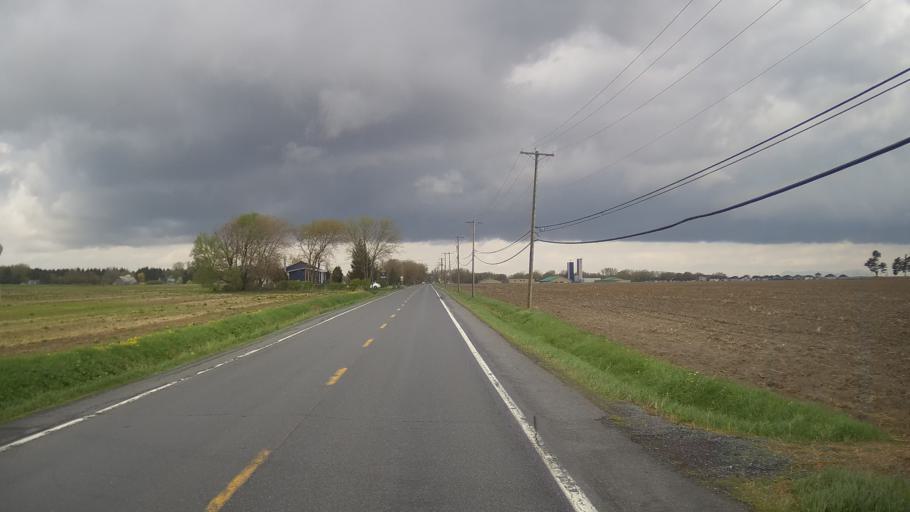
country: CA
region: Quebec
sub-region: Monteregie
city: Farnham
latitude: 45.3153
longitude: -73.0536
